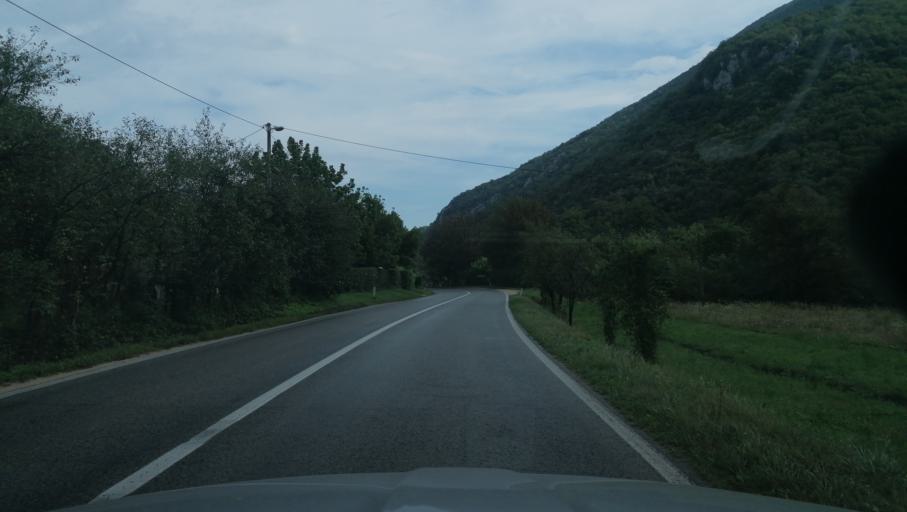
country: BA
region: Republika Srpska
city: Hiseti
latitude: 44.6449
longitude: 17.1465
